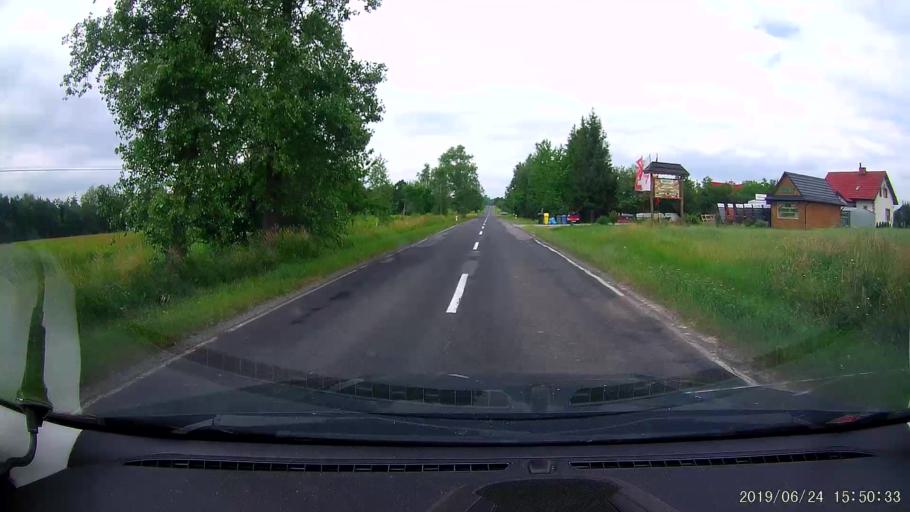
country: PL
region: Subcarpathian Voivodeship
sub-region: Powiat lubaczowski
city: Oleszyce
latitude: 50.1787
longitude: 23.0601
